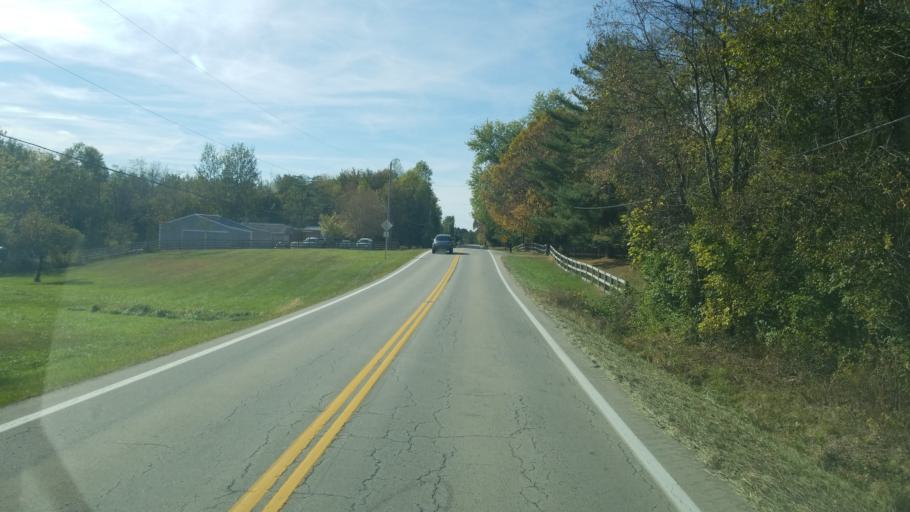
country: US
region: Ohio
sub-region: Clinton County
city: Blanchester
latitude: 39.3801
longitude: -83.9375
